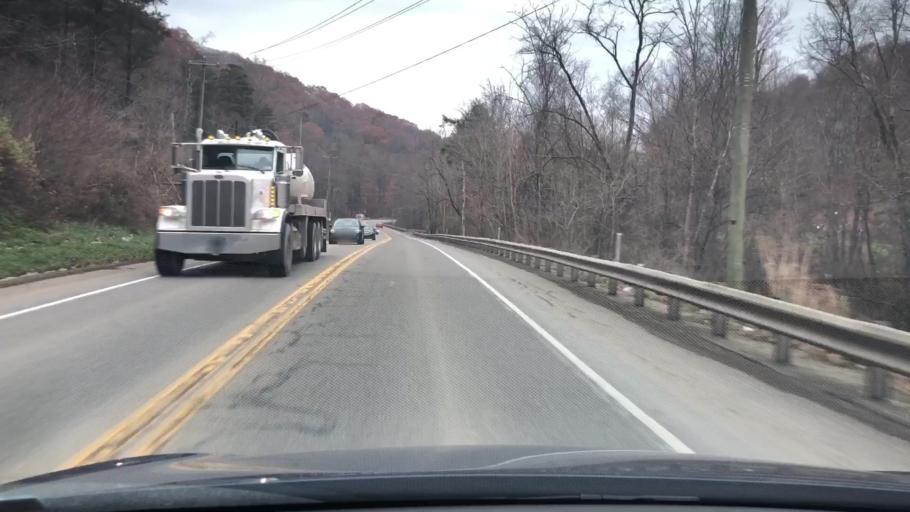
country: US
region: Pennsylvania
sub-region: Clarion County
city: Clarion
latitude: 40.9955
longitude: -79.3422
